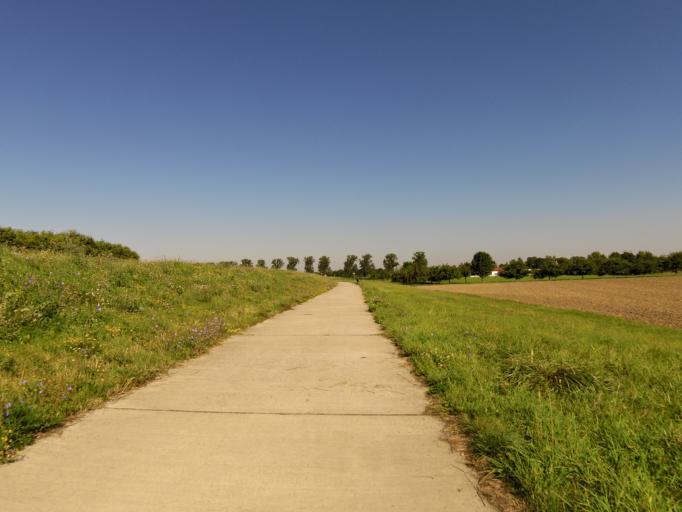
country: DE
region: Hesse
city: Biebesheim
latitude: 49.7719
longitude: 8.4615
